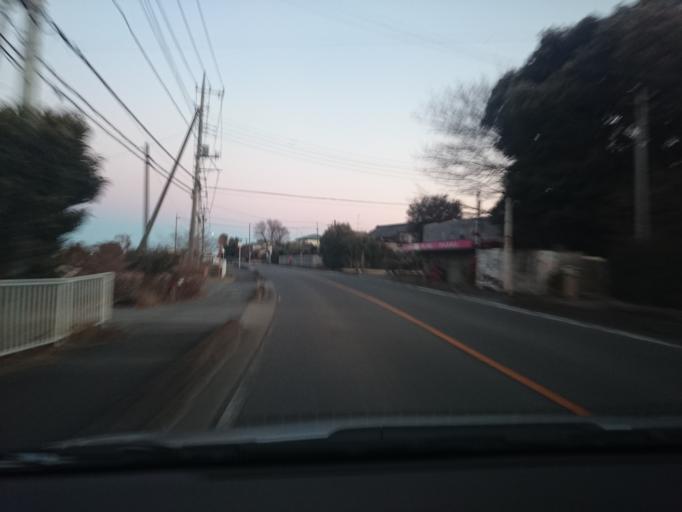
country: JP
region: Saitama
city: Fukayacho
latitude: 36.2280
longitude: 139.3182
